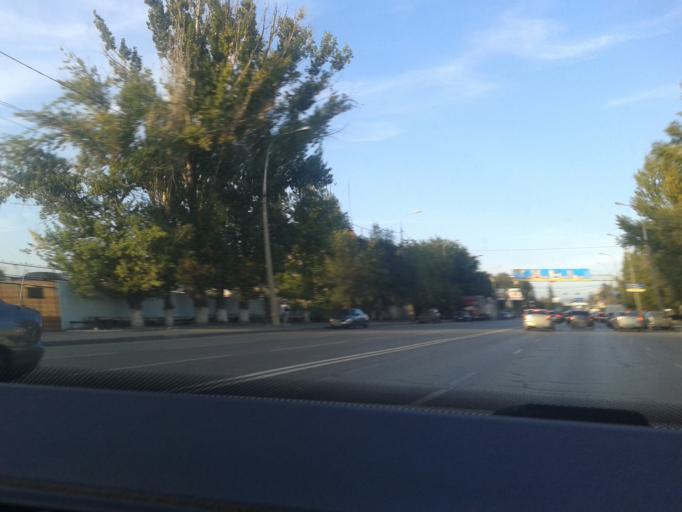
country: RU
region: Volgograd
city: Volgograd
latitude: 48.7123
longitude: 44.4954
